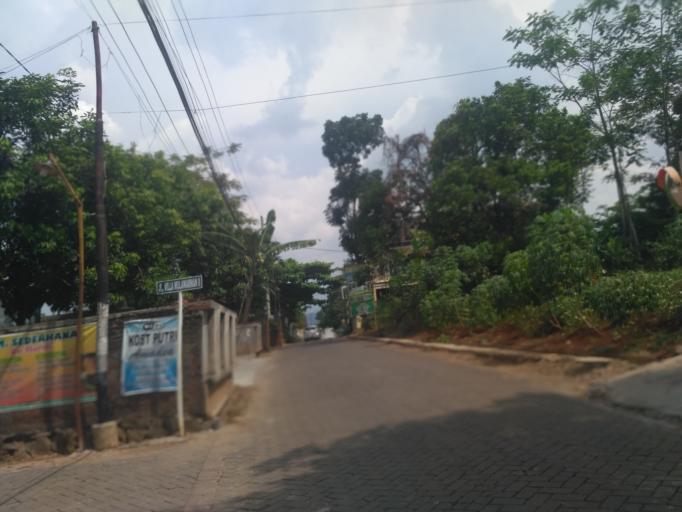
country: ID
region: Central Java
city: Ungaran
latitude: -7.0724
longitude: 110.4407
